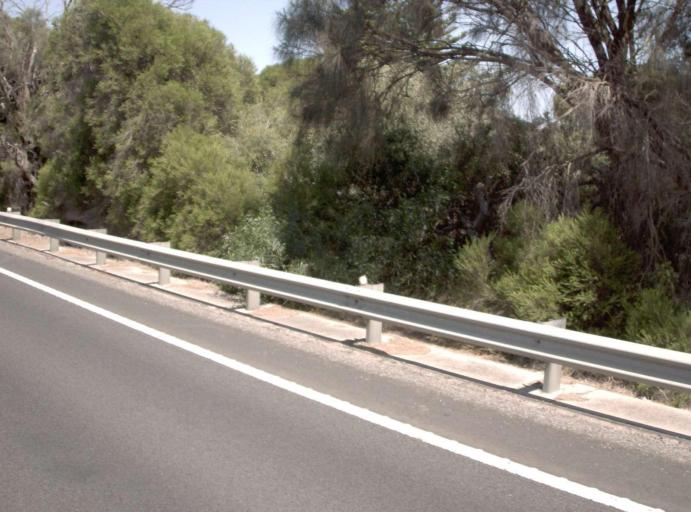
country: AU
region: Victoria
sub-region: Frankston
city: Seaford
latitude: -38.1111
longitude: 145.1385
